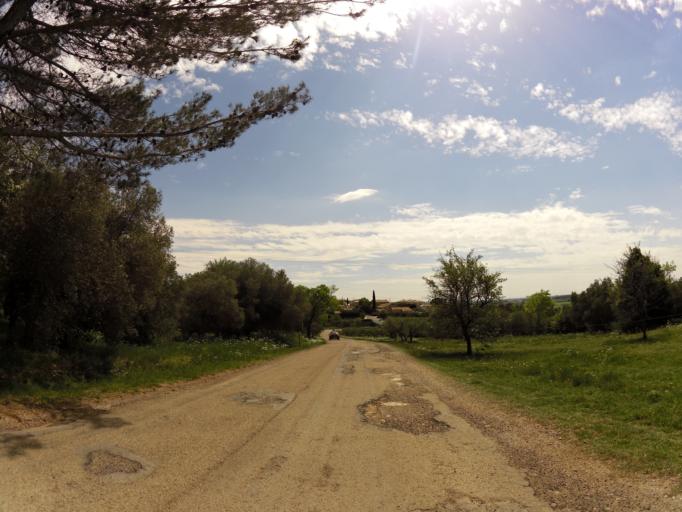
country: FR
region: Languedoc-Roussillon
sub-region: Departement du Gard
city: Gallargues-le-Montueux
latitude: 43.7266
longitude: 4.1720
